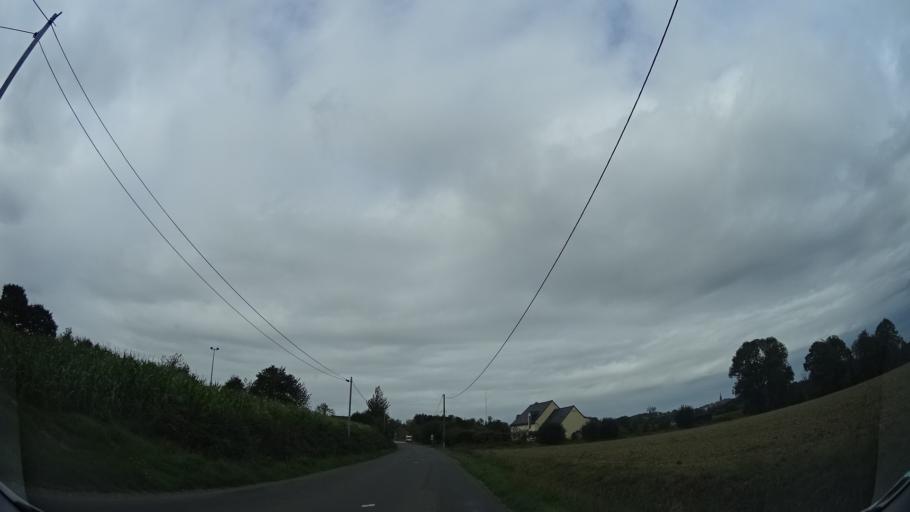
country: FR
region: Brittany
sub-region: Departement d'Ille-et-Vilaine
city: Irodouer
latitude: 48.2860
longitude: -1.9247
